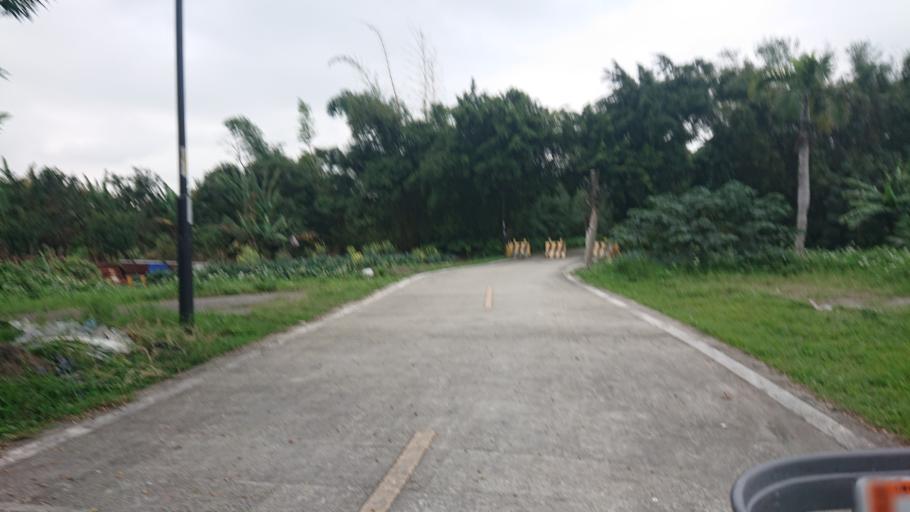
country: TW
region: Taiwan
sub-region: Taoyuan
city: Taoyuan
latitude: 24.9504
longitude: 121.3643
